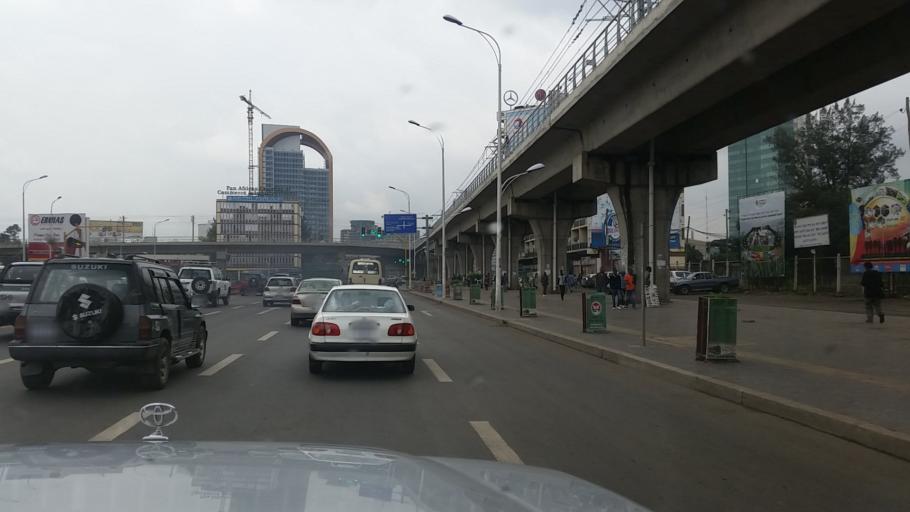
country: ET
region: Adis Abeba
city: Addis Ababa
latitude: 9.0113
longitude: 38.7610
